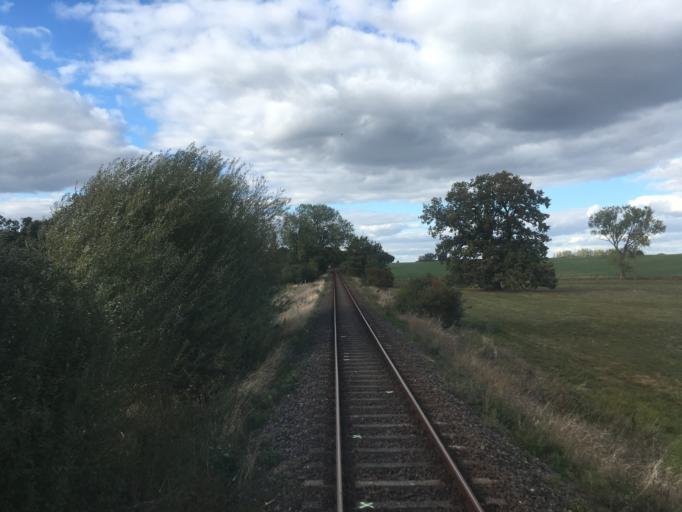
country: DE
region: Mecklenburg-Vorpommern
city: Malchow
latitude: 53.5024
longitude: 12.4284
